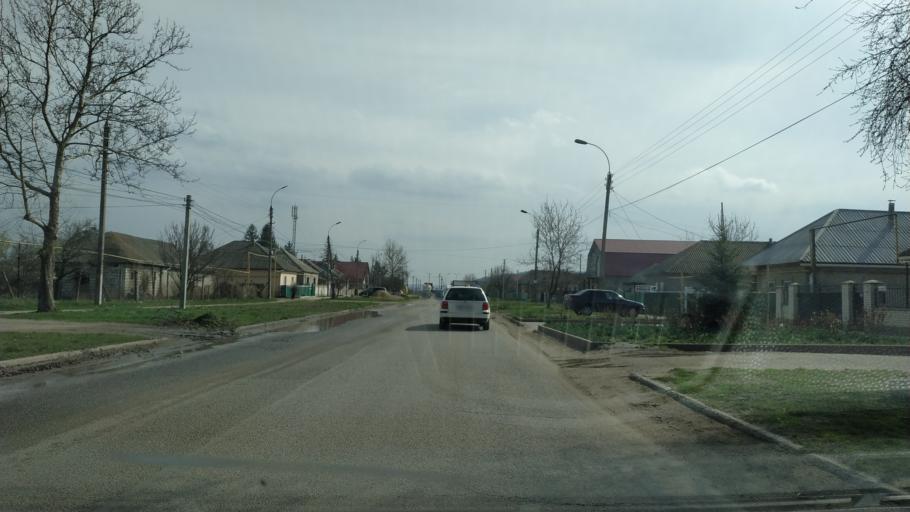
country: MD
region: Gagauzia
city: Vulcanesti
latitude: 45.6792
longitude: 28.4099
